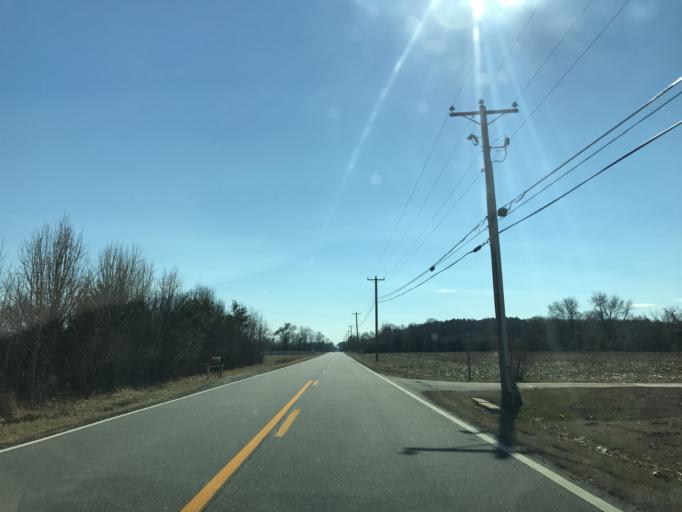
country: US
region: Maryland
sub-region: Queen Anne's County
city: Stevensville
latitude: 39.0199
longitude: -76.3114
